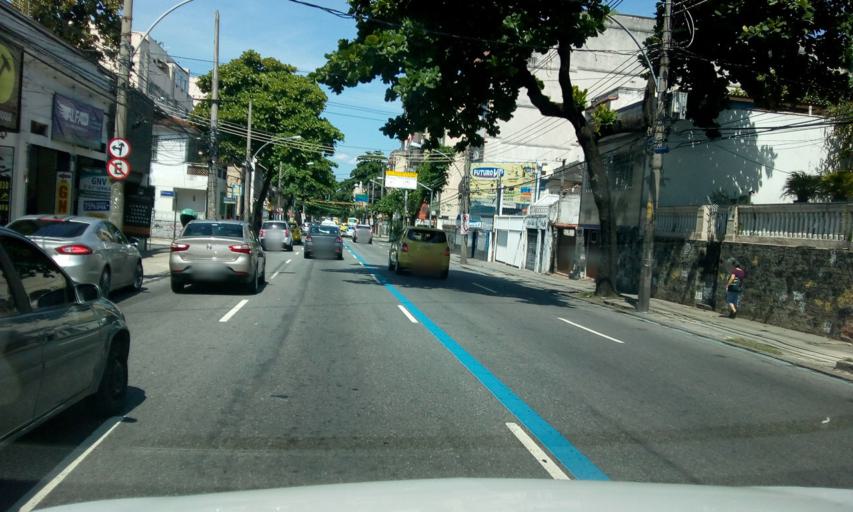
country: BR
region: Rio de Janeiro
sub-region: Rio De Janeiro
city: Rio de Janeiro
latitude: -22.9179
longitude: -43.2468
